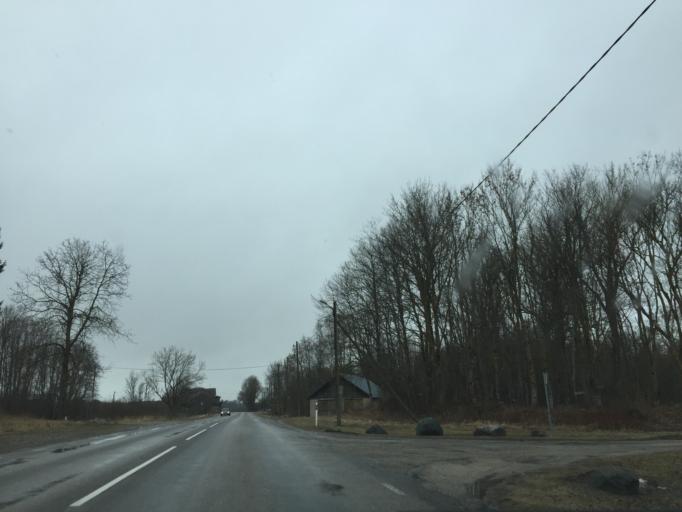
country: EE
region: Laeaene
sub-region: Ridala Parish
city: Uuemoisa
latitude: 58.8657
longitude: 23.6233
